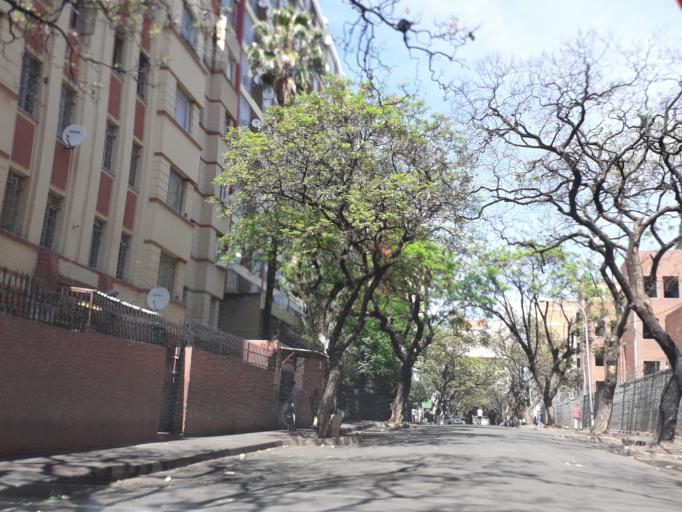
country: ZA
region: Gauteng
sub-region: City of Johannesburg Metropolitan Municipality
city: Johannesburg
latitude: -26.1900
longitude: 28.0530
